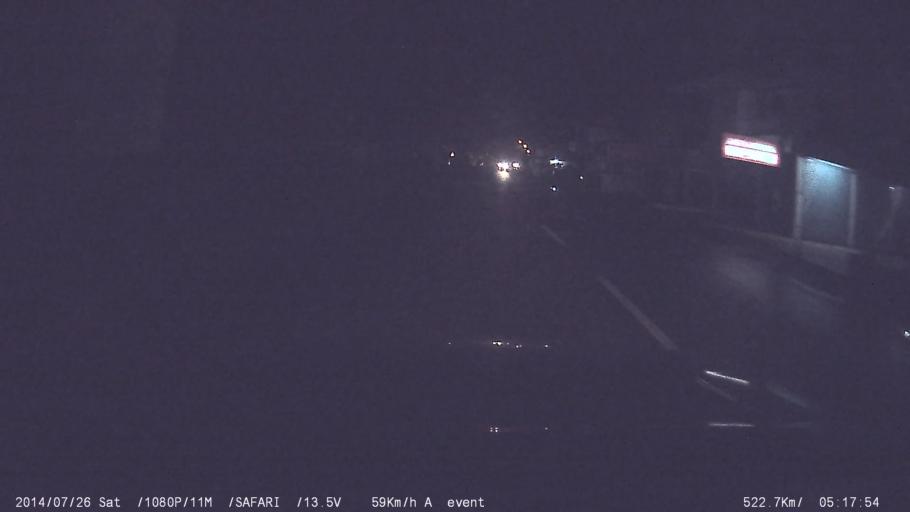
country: IN
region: Kerala
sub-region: Ernakulam
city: Muvattupula
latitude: 10.0122
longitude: 76.5677
